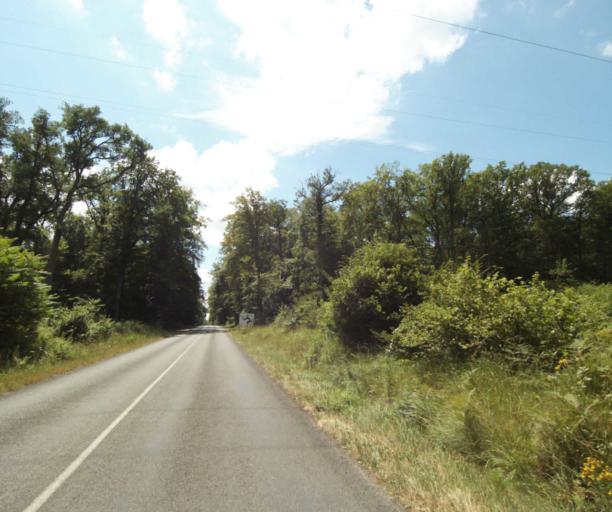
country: FR
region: Ile-de-France
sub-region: Departement de Seine-et-Marne
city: Samoreau
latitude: 48.4357
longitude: 2.7417
